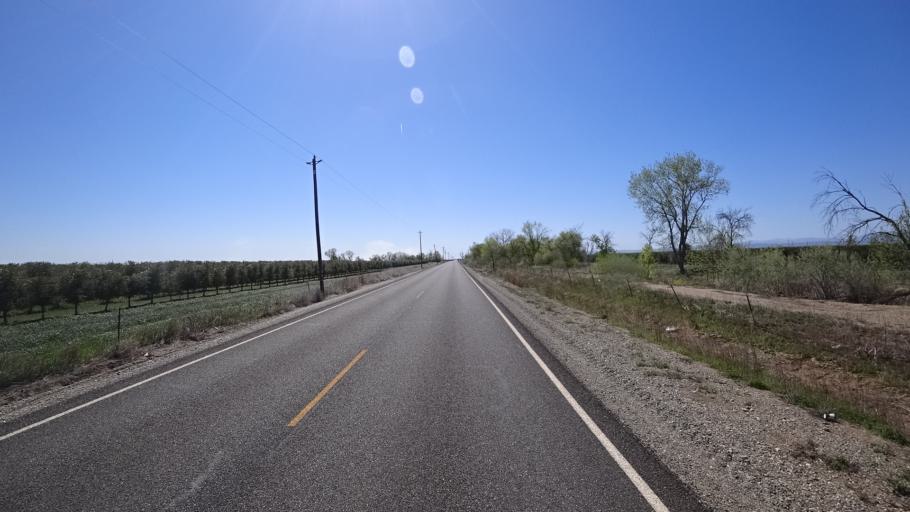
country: US
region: California
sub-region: Glenn County
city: Willows
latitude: 39.6083
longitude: -122.2499
